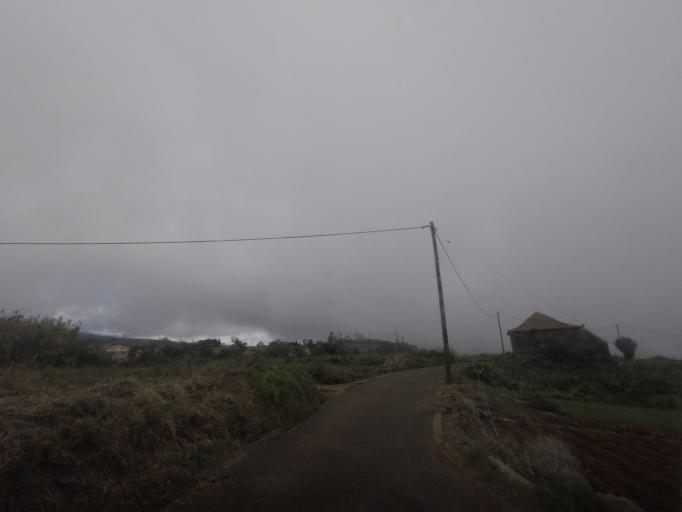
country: PT
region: Madeira
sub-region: Calheta
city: Faja da Ovelha
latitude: 32.7631
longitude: -17.2170
